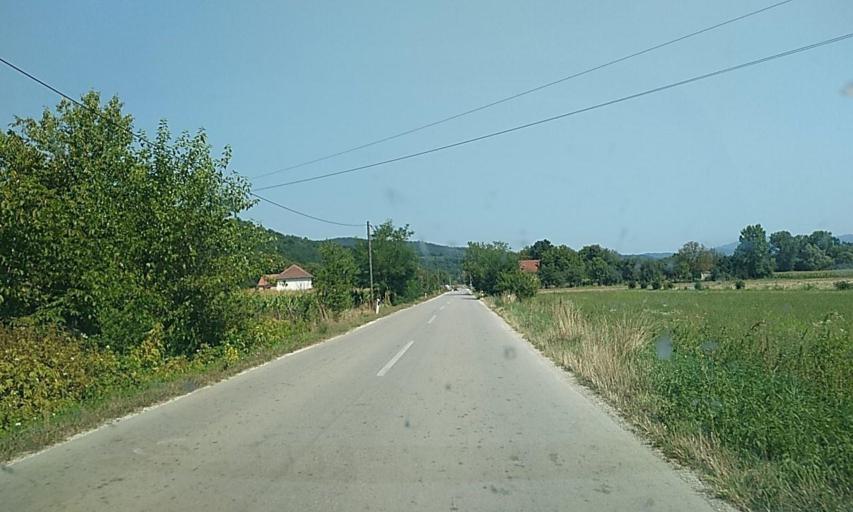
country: RS
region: Central Serbia
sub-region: Pcinjski Okrug
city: Vladicin Han
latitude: 42.6638
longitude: 22.0460
